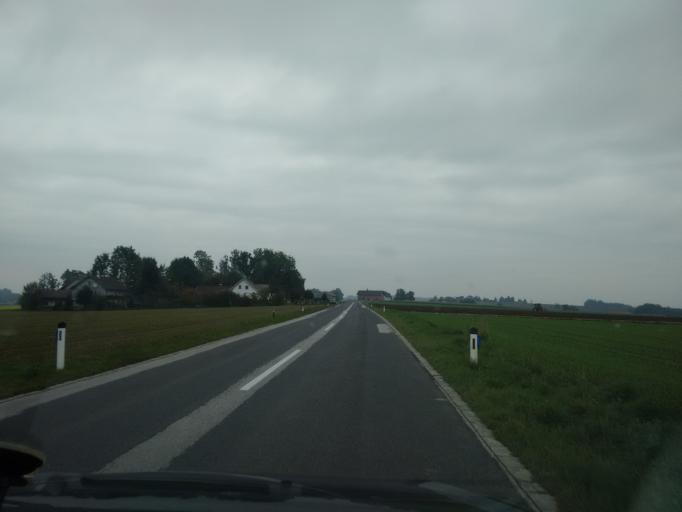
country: AT
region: Upper Austria
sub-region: Politischer Bezirk Kirchdorf an der Krems
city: Kremsmunster
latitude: 48.0373
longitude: 14.0943
